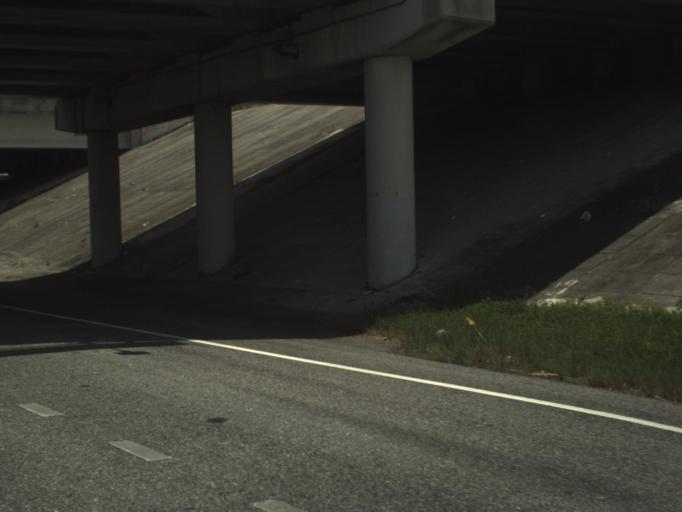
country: US
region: Florida
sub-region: Martin County
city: Palm City
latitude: 27.1091
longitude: -80.2602
